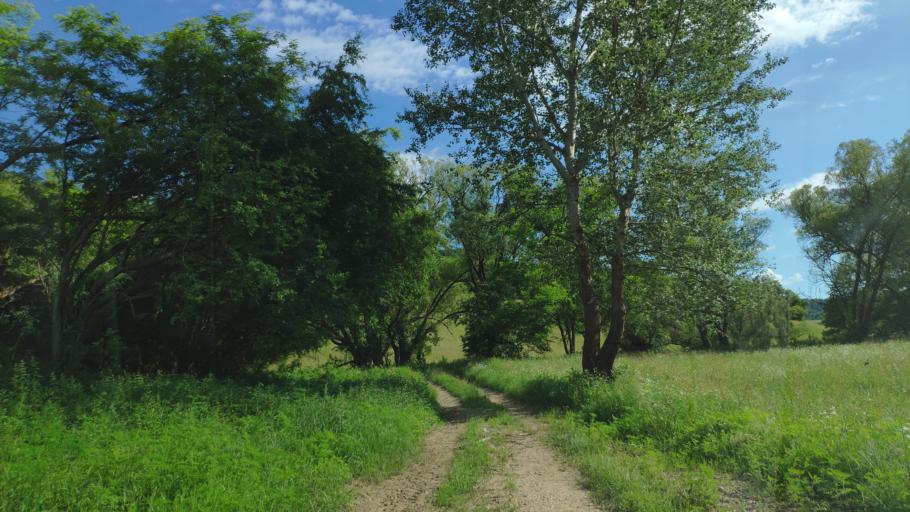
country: SK
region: Banskobystricky
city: Rimavska Sobota
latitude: 48.2537
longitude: 20.1098
